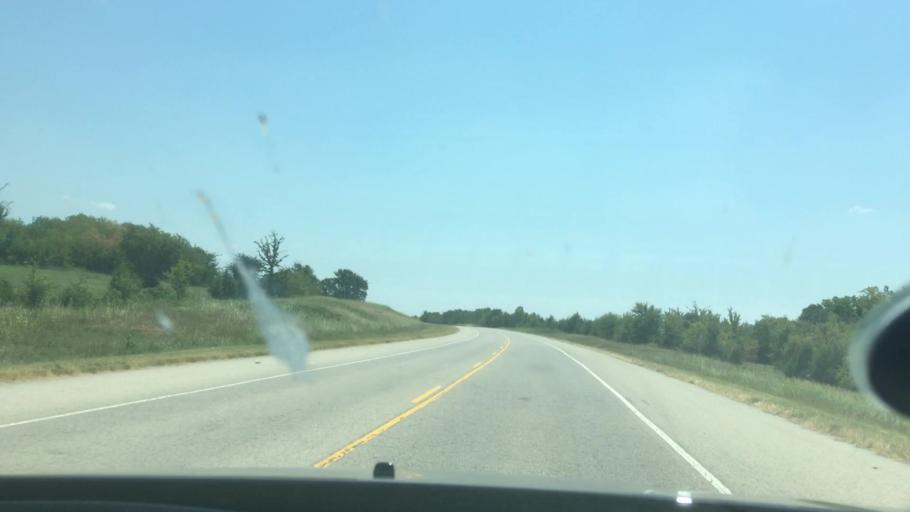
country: US
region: Oklahoma
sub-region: Pontotoc County
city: Ada
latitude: 34.6473
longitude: -96.5508
